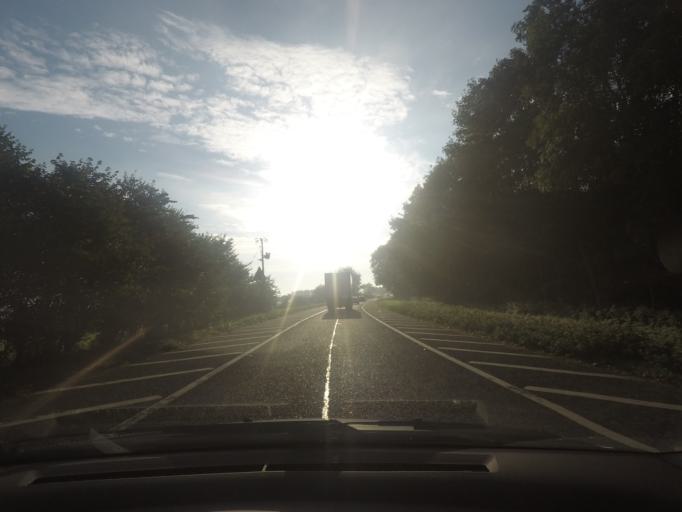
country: GB
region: England
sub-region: East Riding of Yorkshire
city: Hayton
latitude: 53.8881
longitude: -0.7284
